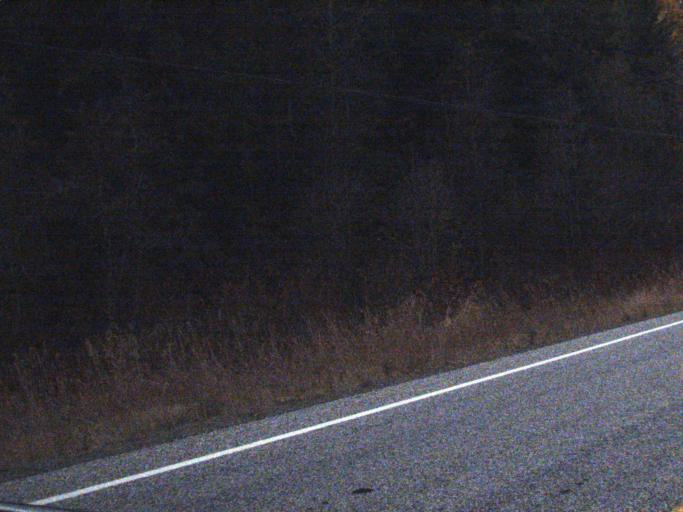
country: US
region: Washington
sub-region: Ferry County
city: Republic
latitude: 48.6261
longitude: -118.6750
